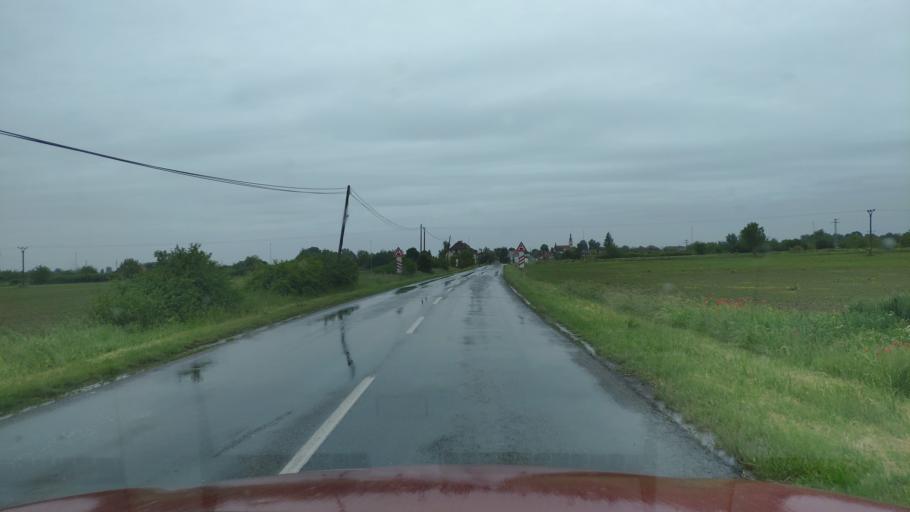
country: SK
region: Kosicky
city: Cierna nad Tisou
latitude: 48.4186
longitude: 22.0268
